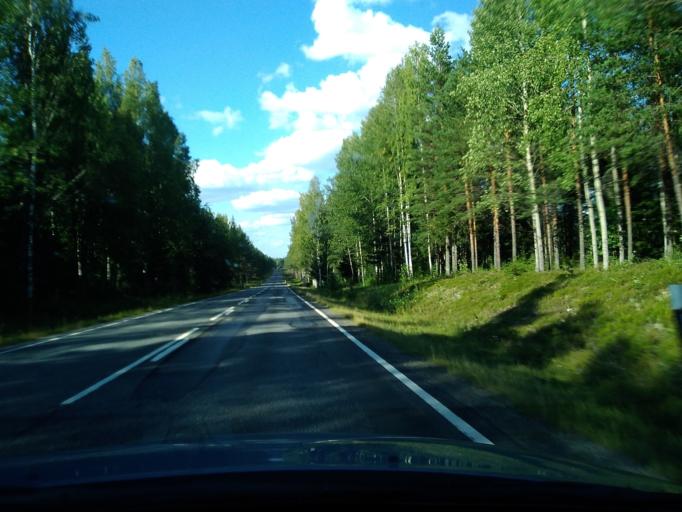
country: FI
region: Pirkanmaa
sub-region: Ylae-Pirkanmaa
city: Vilppula
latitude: 61.9369
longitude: 24.5406
